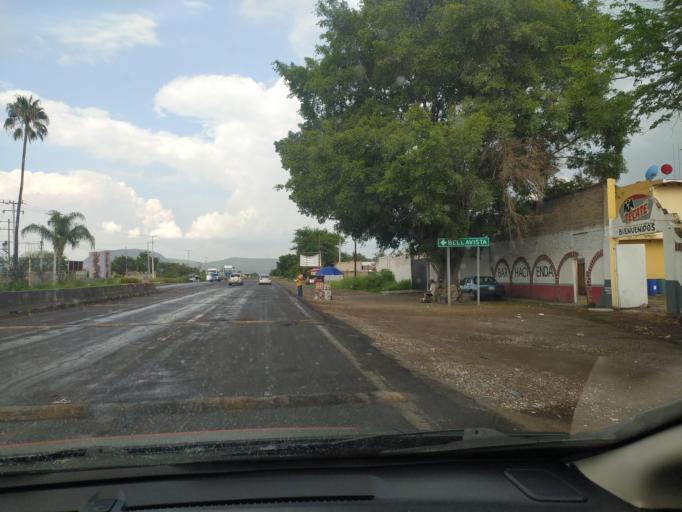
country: MX
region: Jalisco
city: Bellavista
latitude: 20.4162
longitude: -103.6273
